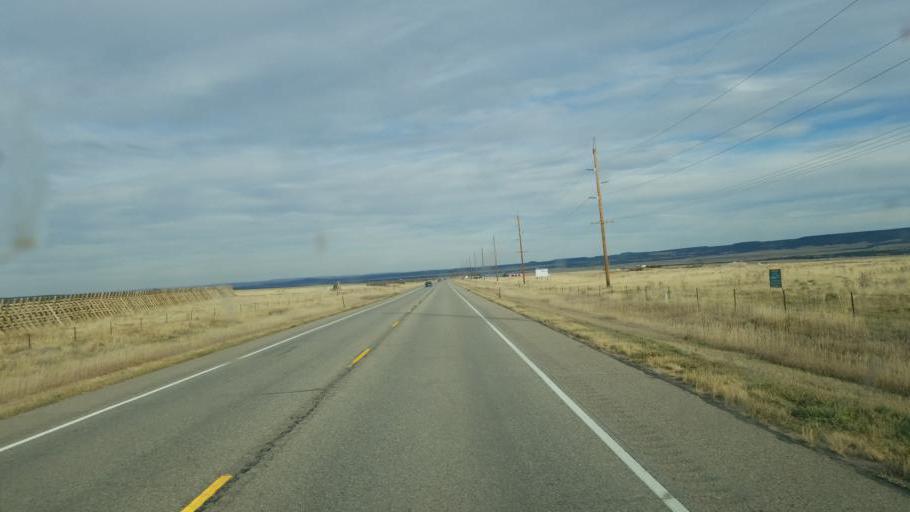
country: US
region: Colorado
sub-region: Huerfano County
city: Walsenburg
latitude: 37.5422
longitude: -105.0457
